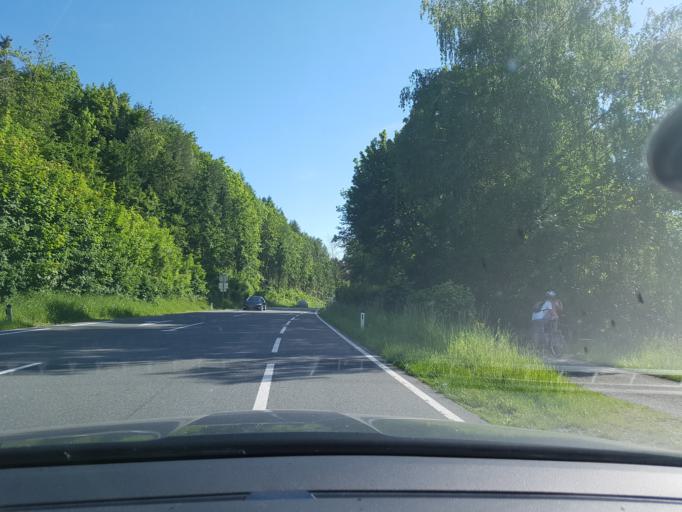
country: AT
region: Salzburg
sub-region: Politischer Bezirk Salzburg-Umgebung
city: Mattsee
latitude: 47.9630
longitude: 13.0968
